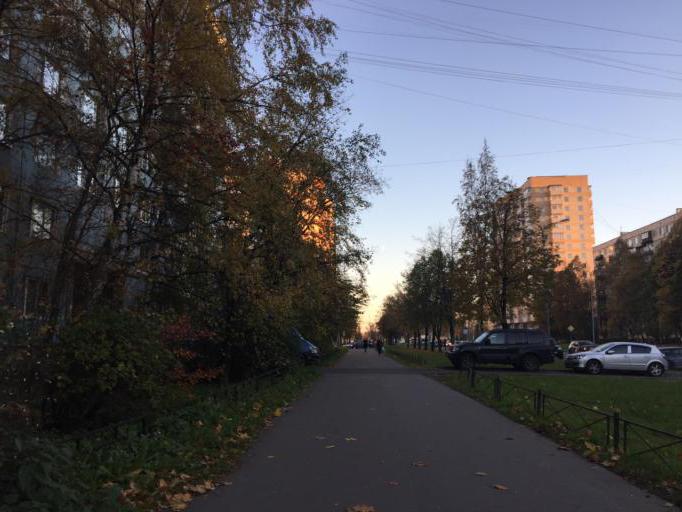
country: RU
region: St.-Petersburg
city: Obukhovo
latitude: 59.9002
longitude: 30.4724
